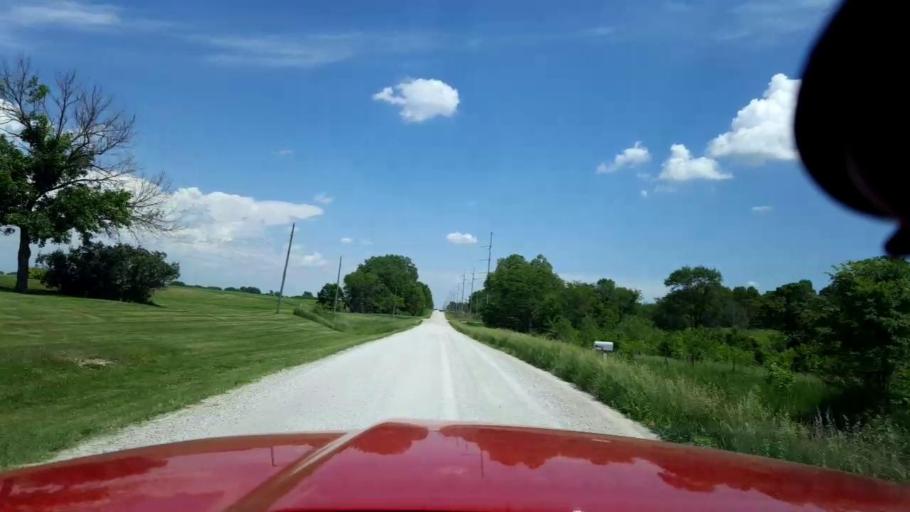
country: US
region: Iowa
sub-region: Boone County
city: Boone
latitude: 42.0492
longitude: -93.7595
